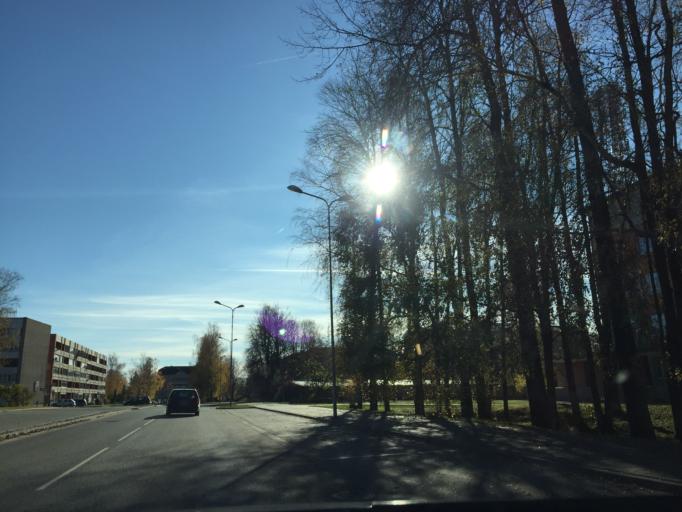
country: LV
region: Aizkraukles Rajons
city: Aizkraukle
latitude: 56.6035
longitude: 25.2550
